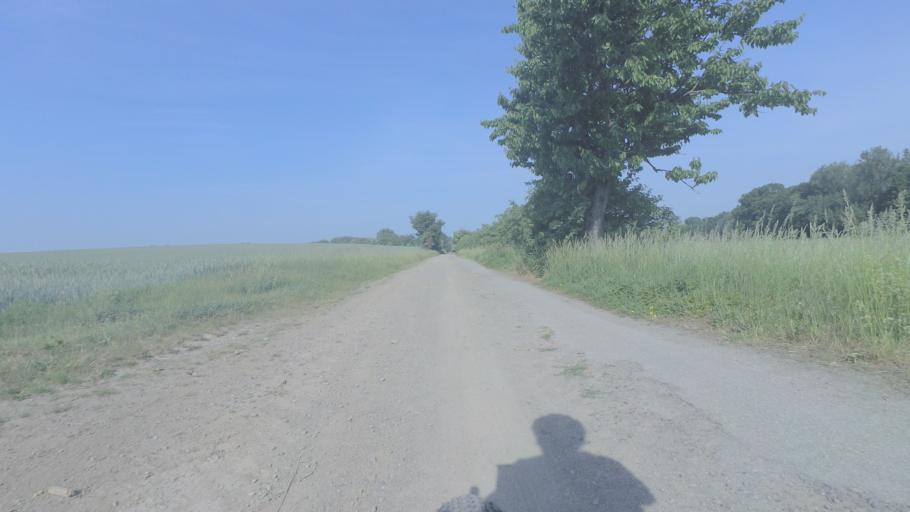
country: DE
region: Saxony-Anhalt
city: Hoym
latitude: 51.7676
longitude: 11.3394
